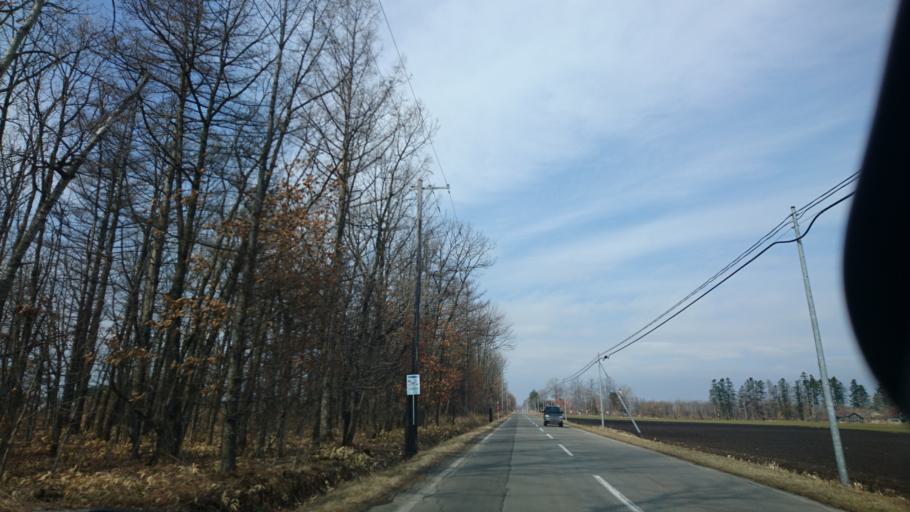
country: JP
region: Hokkaido
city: Otofuke
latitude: 43.0801
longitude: 143.2318
